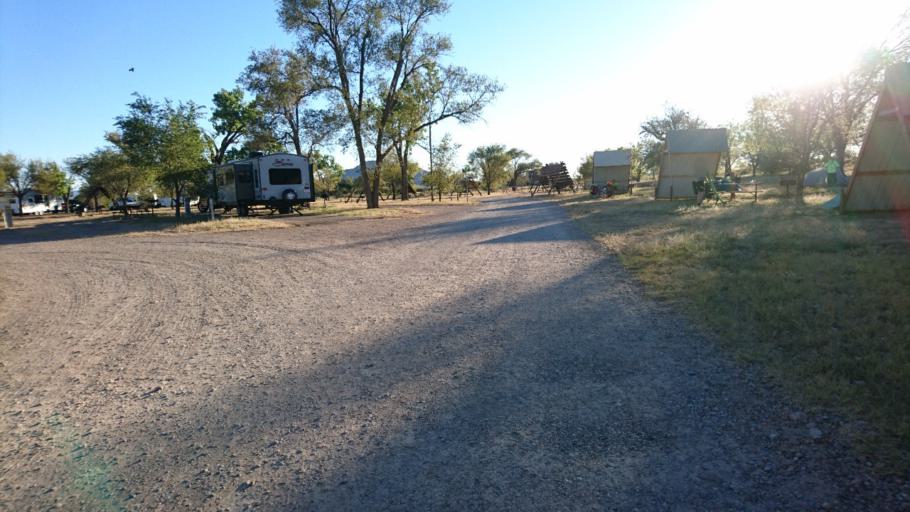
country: US
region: New Mexico
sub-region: Quay County
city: Tucumcari
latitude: 35.1711
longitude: -103.6683
